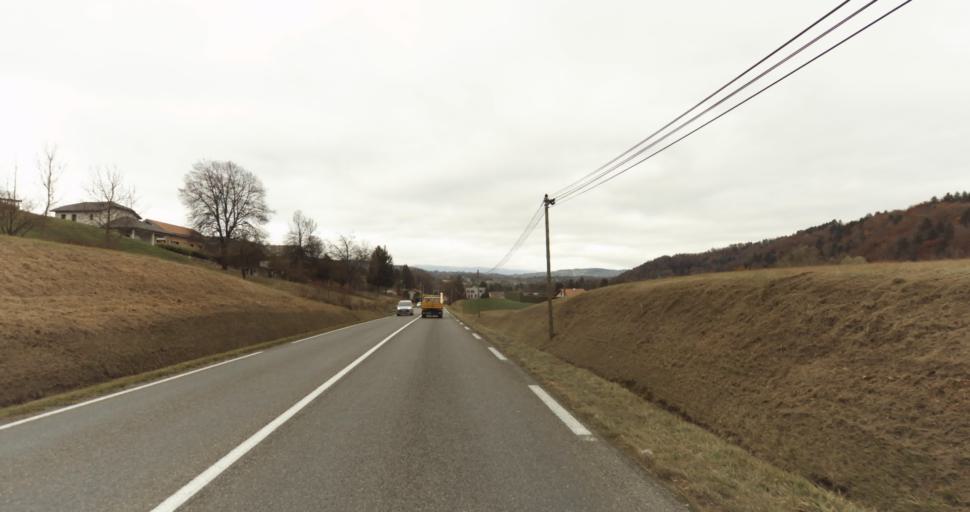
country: FR
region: Rhone-Alpes
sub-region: Departement de la Haute-Savoie
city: Saint-Martin-Bellevue
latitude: 45.9652
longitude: 6.1647
